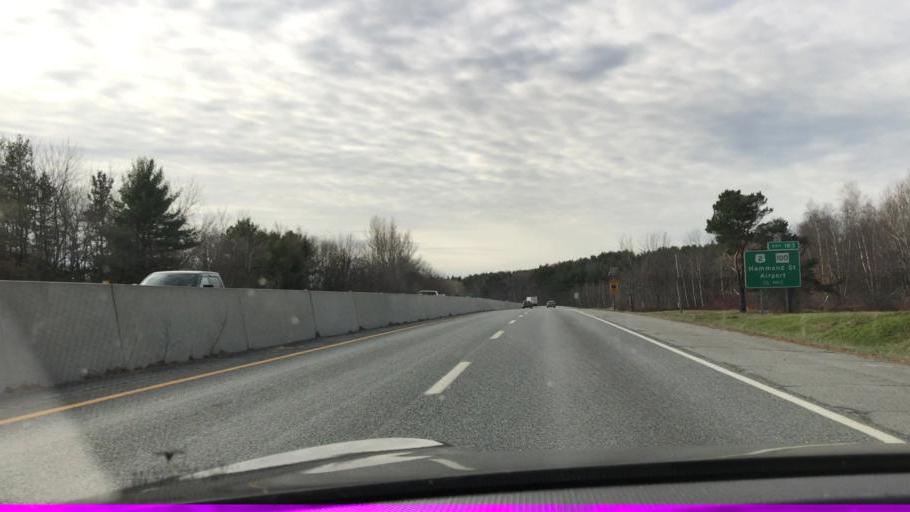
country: US
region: Maine
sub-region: Penobscot County
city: Bangor
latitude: 44.8058
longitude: -68.7967
